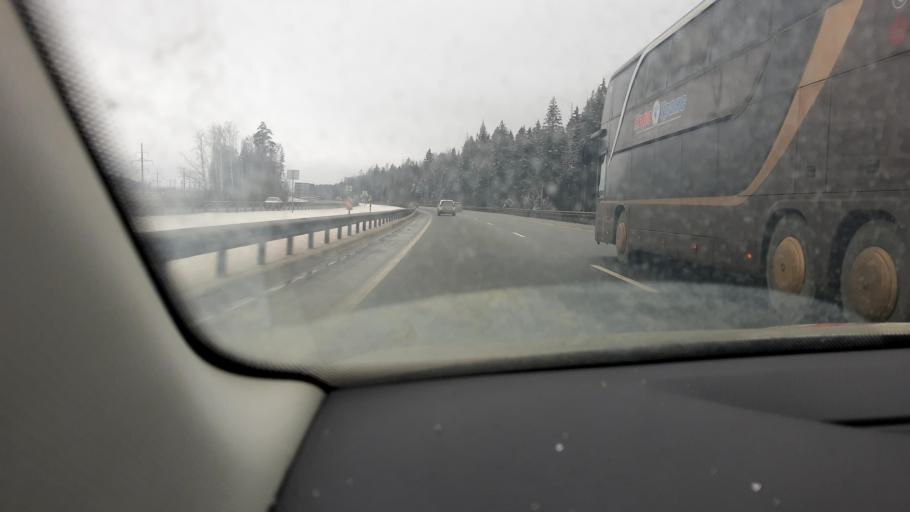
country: RU
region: Moskovskaya
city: Mikhnevo
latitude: 55.0675
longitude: 37.9308
